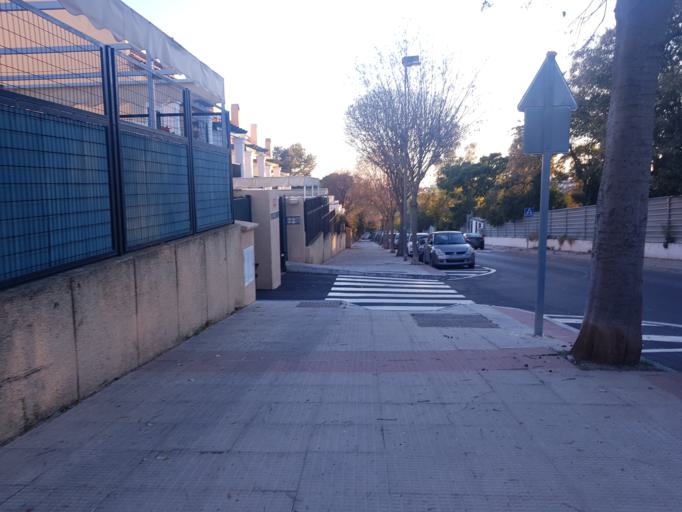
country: ES
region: Andalusia
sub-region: Provincia de Malaga
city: Marbella
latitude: 36.5258
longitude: -4.8904
